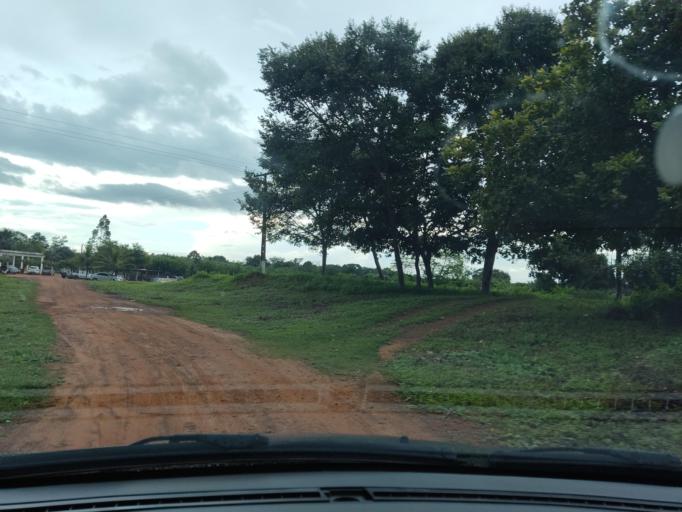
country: BR
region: Piaui
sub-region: Valenca Do Piaui
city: Valenca do Piaui
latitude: -6.3537
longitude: -41.7071
